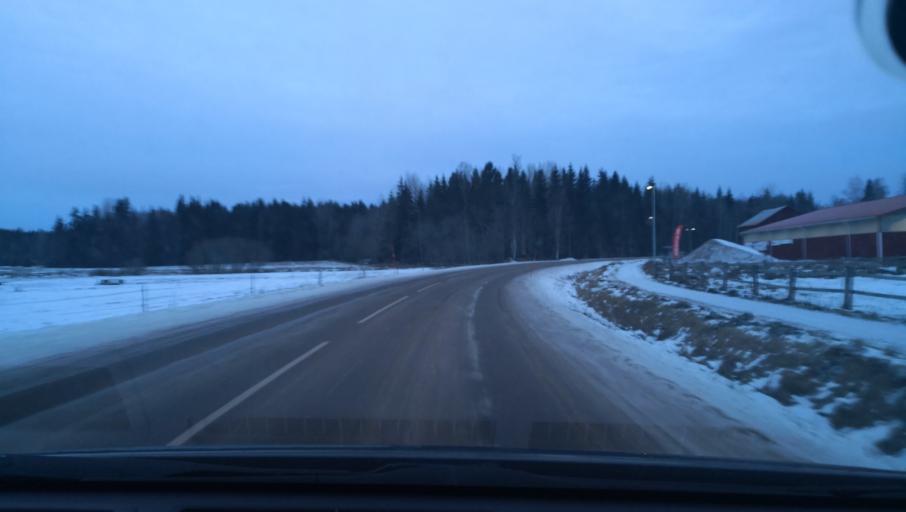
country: SE
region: Dalarna
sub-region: Avesta Kommun
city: Horndal
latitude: 60.1984
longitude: 16.4617
